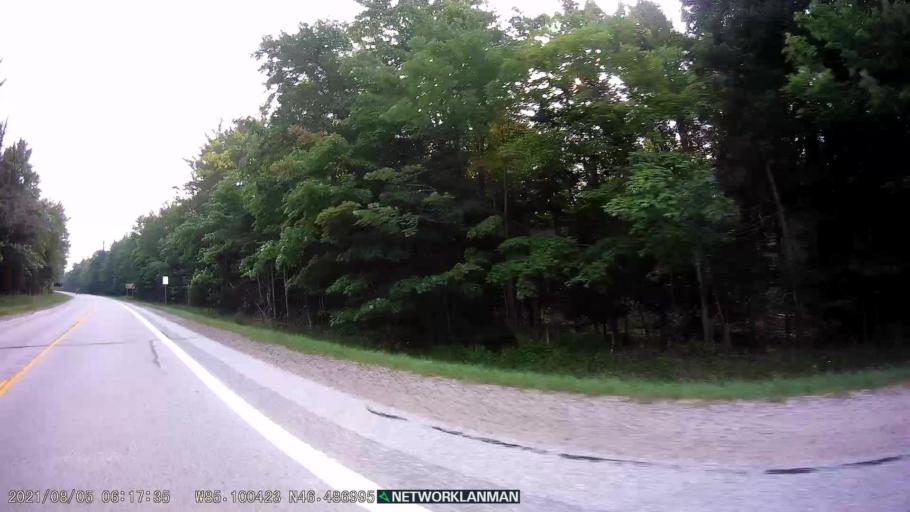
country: US
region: Michigan
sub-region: Luce County
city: Newberry
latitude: 46.4879
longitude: -85.0999
